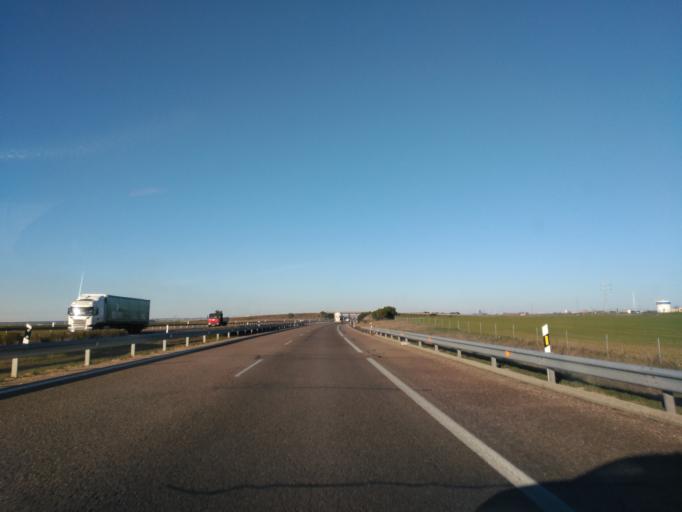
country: ES
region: Castille and Leon
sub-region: Provincia de Salamanca
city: Castellanos de Moriscos
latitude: 41.0244
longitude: -5.5777
